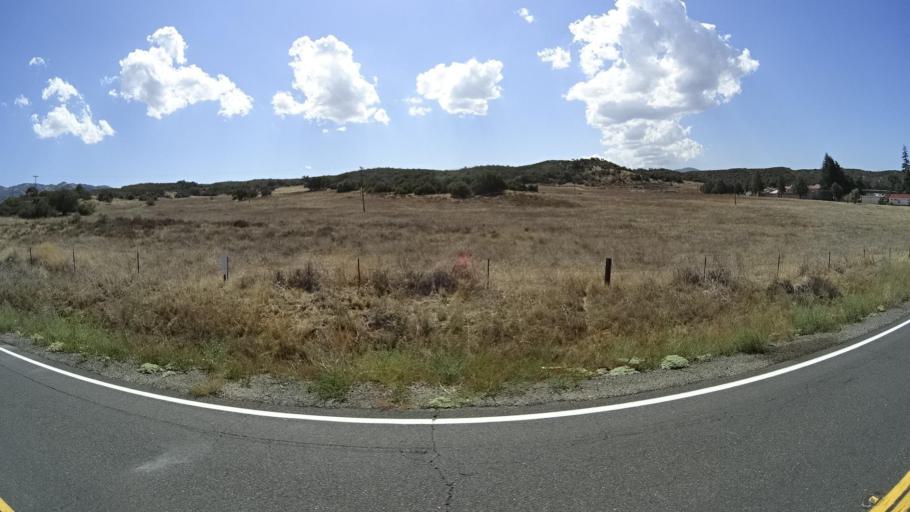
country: US
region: California
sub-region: San Diego County
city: Julian
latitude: 33.2766
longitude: -116.6415
